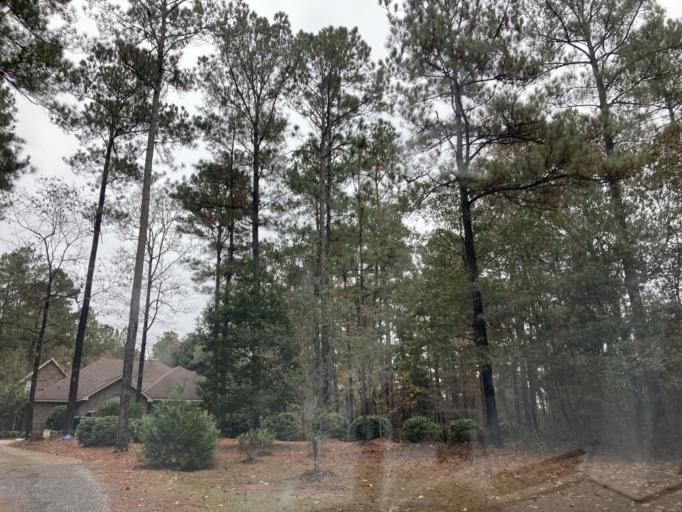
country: US
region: Mississippi
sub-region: Lamar County
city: Purvis
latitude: 31.1916
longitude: -89.4244
